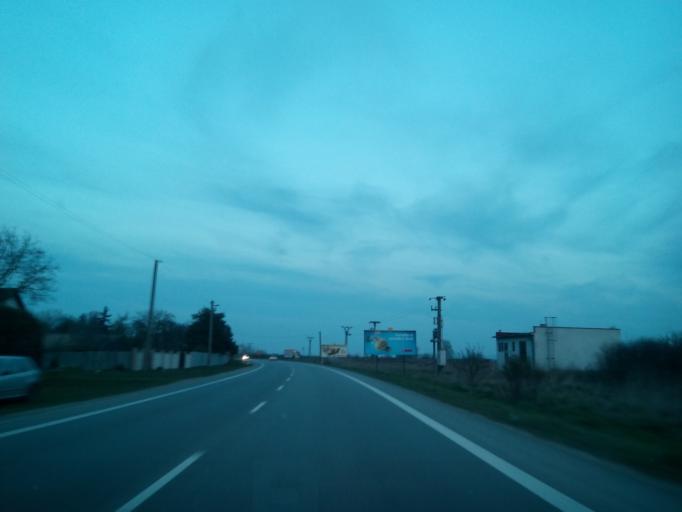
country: SK
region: Kosicky
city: Moldava nad Bodvou
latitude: 48.6064
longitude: 20.9532
